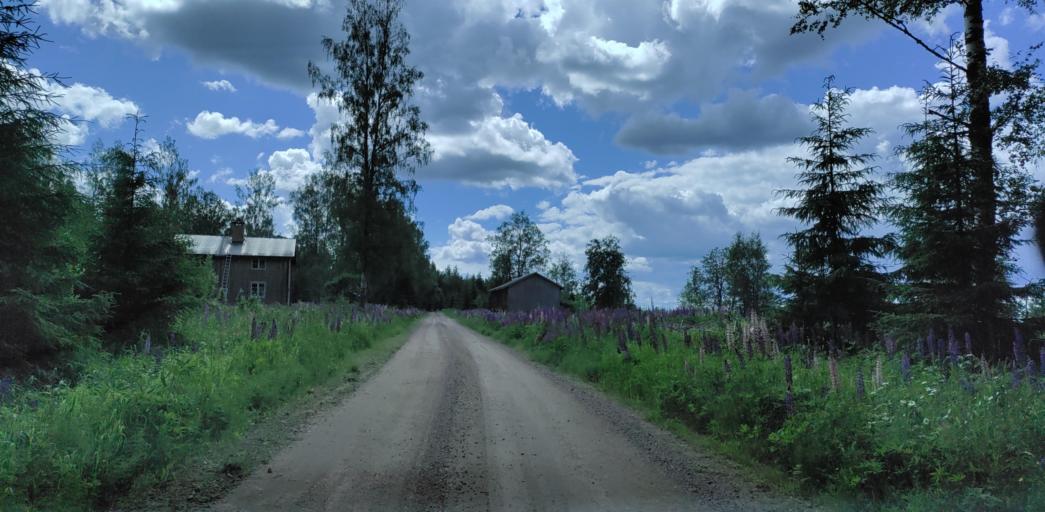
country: SE
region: Vaermland
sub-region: Hagfors Kommun
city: Ekshaerad
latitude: 60.0824
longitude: 13.3142
